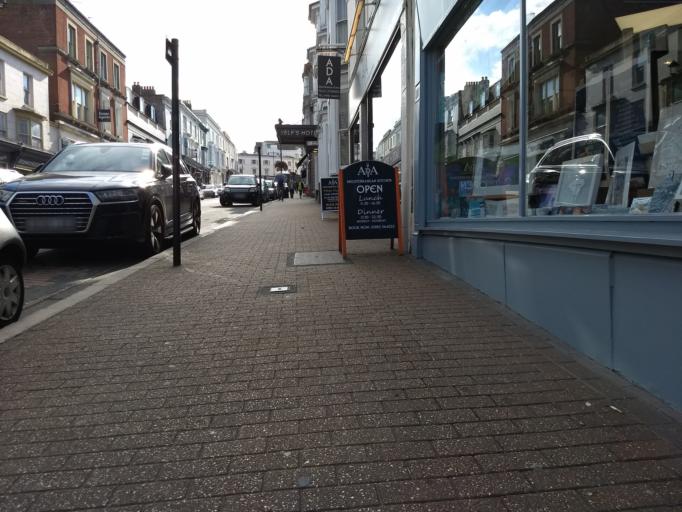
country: GB
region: England
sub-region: Isle of Wight
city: Ryde
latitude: 50.7312
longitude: -1.1621
